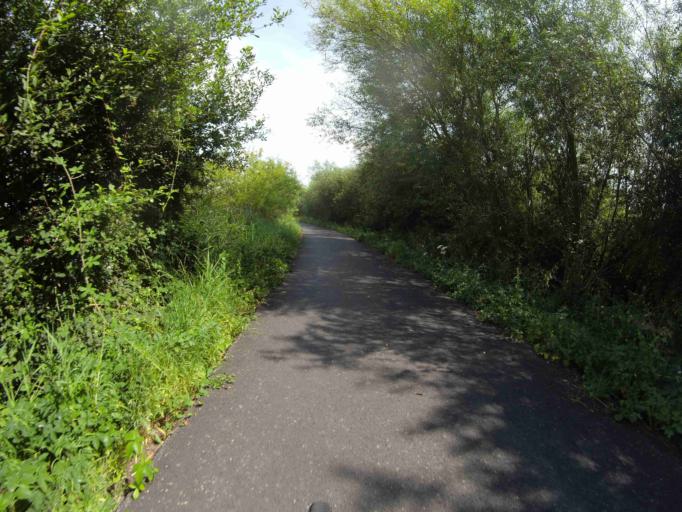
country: GB
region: England
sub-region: Devon
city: Exminster
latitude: 50.6930
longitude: -3.4957
